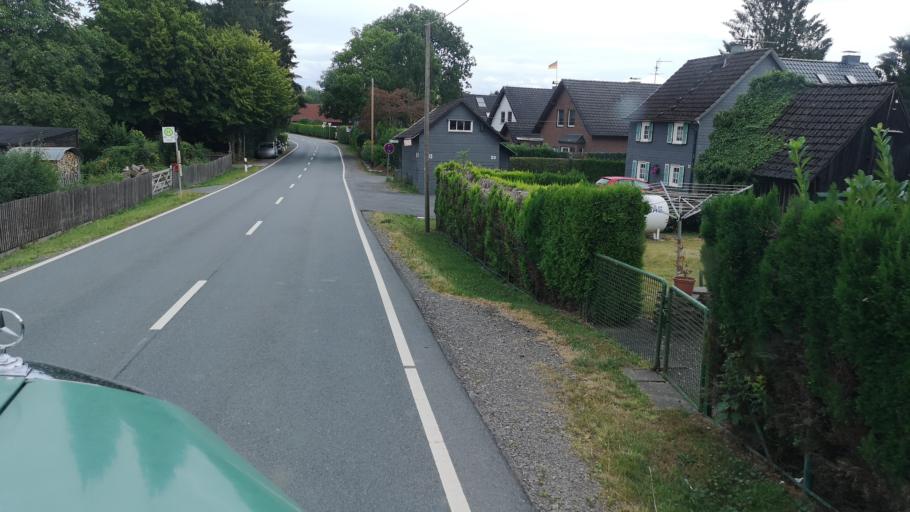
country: DE
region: North Rhine-Westphalia
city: Burscheid
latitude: 51.0820
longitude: 7.1671
